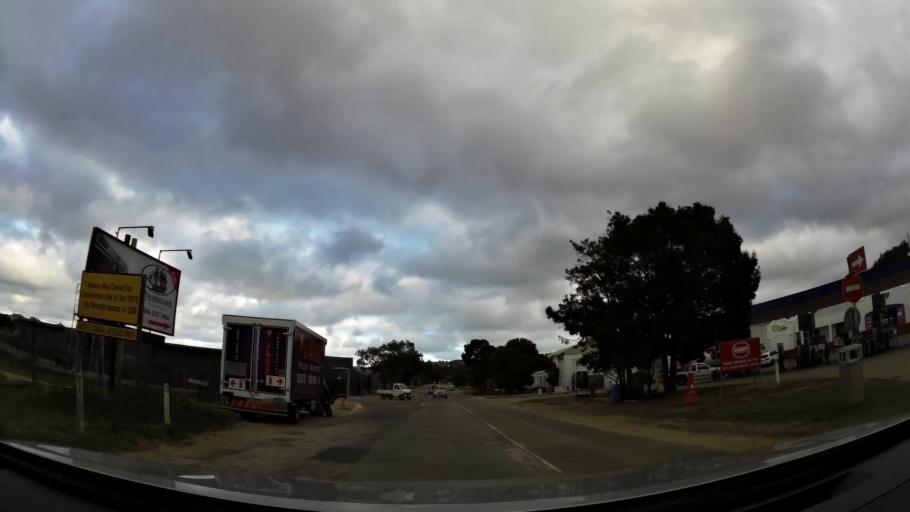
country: ZA
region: Western Cape
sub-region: Eden District Municipality
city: Plettenberg Bay
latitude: -34.0409
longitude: 23.3705
